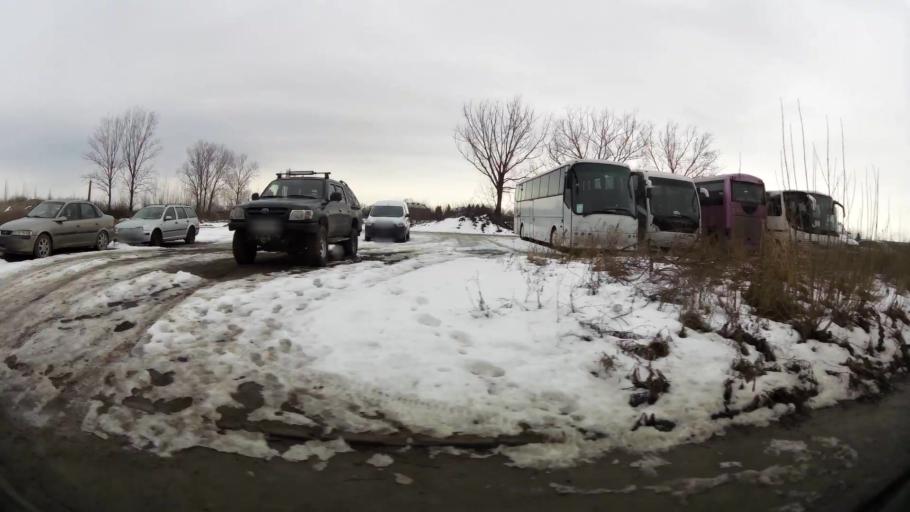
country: RO
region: Ilfov
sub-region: Comuna Pantelimon
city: Pantelimon
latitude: 44.4535
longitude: 26.2122
